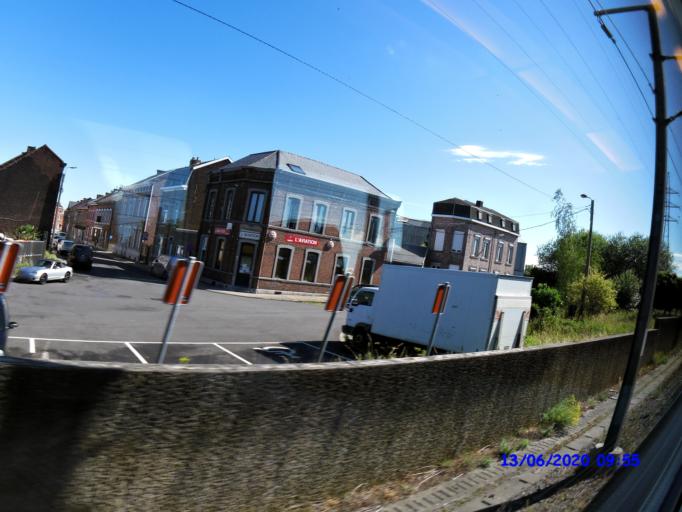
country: BE
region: Wallonia
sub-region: Province de Liege
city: Awans
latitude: 50.6584
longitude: 5.4588
